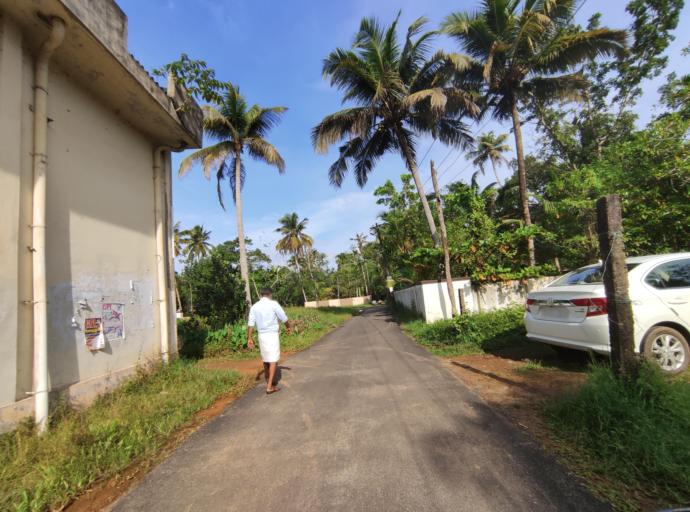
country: IN
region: Kerala
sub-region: Alappuzha
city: Vayalar
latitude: 9.6998
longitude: 76.3372
